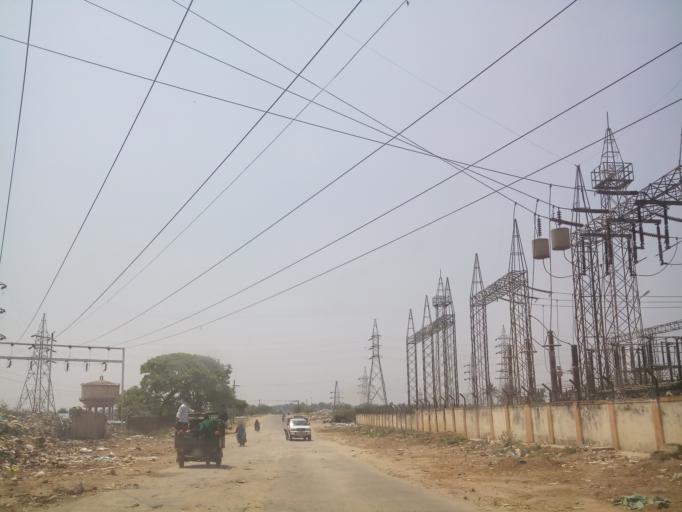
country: IN
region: Karnataka
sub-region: Hassan
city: Hassan
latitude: 12.9974
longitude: 76.0937
